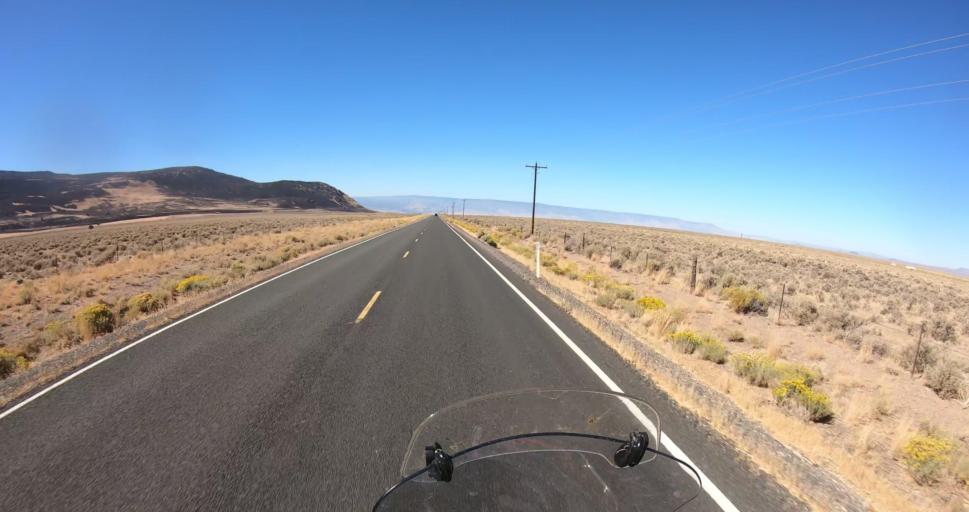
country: US
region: Oregon
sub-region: Lake County
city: Lakeview
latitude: 42.7089
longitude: -120.5593
